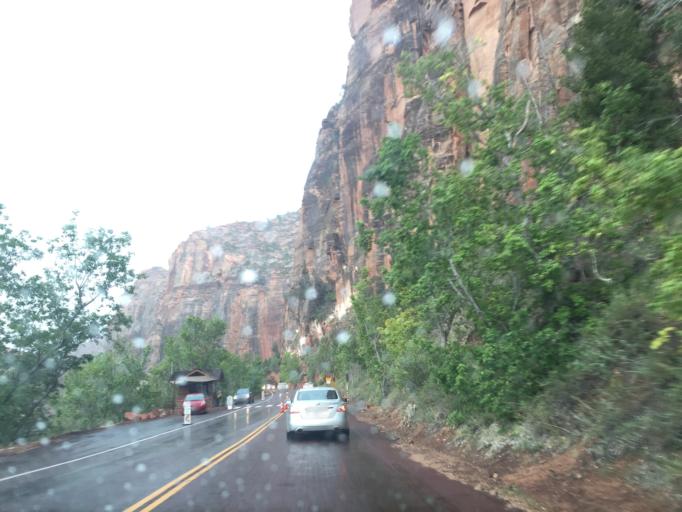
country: US
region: Utah
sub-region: Washington County
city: Hildale
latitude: 37.2121
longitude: -112.9609
